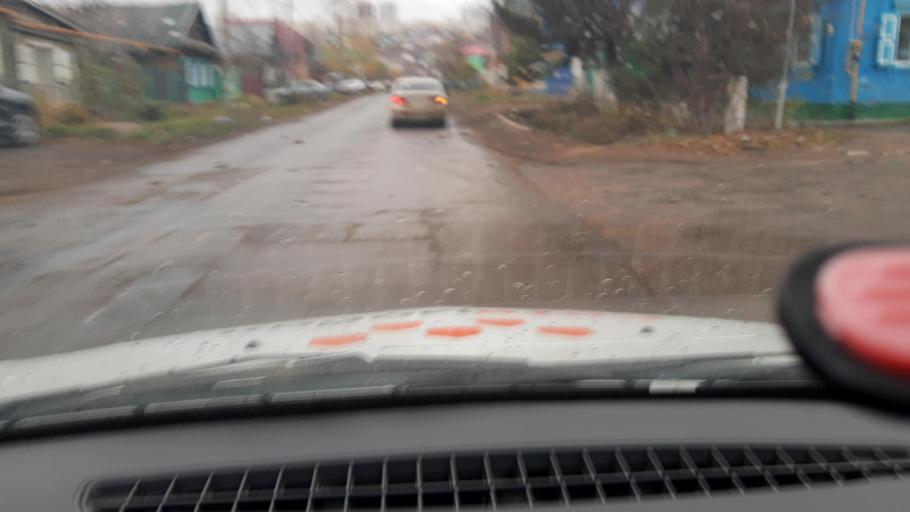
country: RU
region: Bashkortostan
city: Ufa
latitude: 54.7412
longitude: 55.9158
